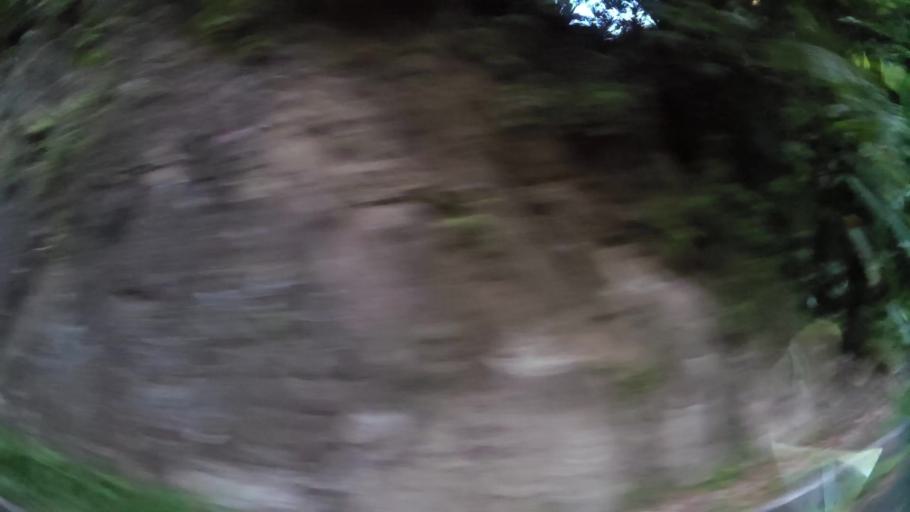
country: DM
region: Saint Andrew
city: Calibishie
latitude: 15.5898
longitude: -61.3982
